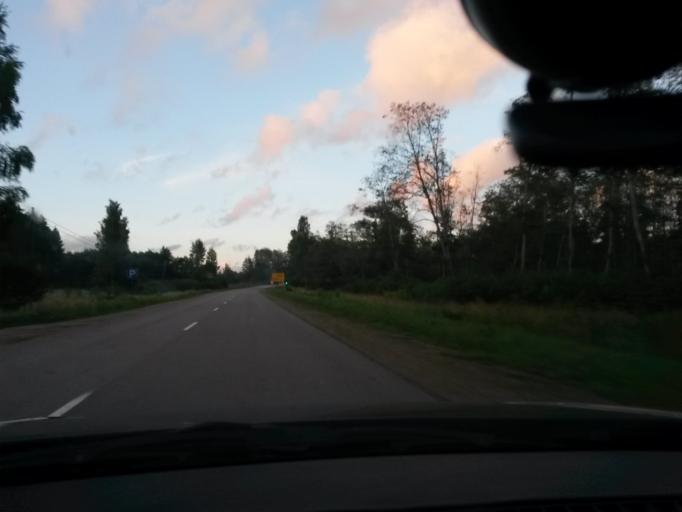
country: LV
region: Madonas Rajons
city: Madona
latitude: 56.8088
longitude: 26.0948
